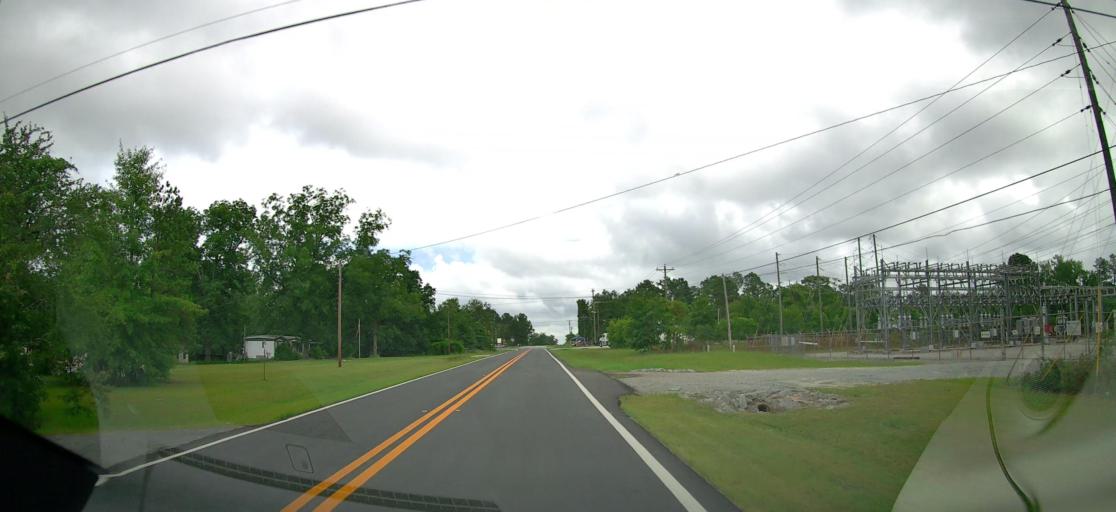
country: US
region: Georgia
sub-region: Bibb County
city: West Point
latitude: 32.7567
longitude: -83.7620
